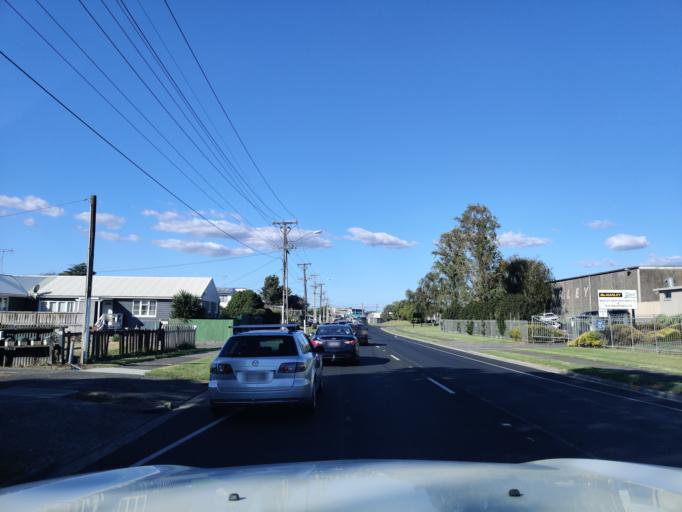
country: NZ
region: Auckland
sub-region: Auckland
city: Takanini
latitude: -37.0342
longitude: 174.9012
